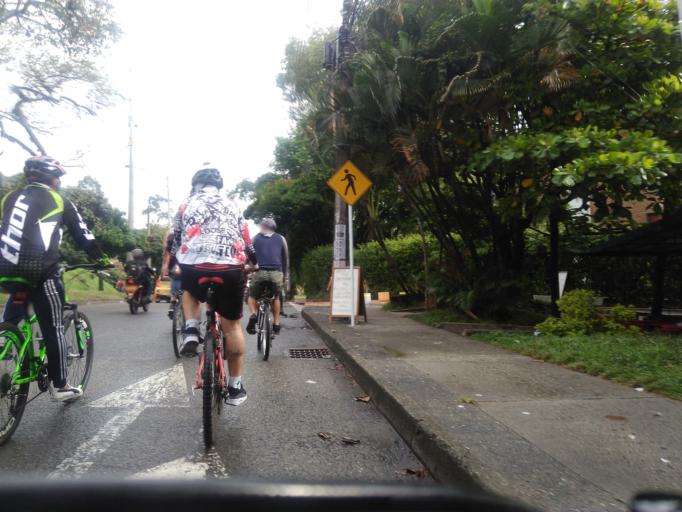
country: CO
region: Antioquia
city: Medellin
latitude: 6.2577
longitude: -75.5804
